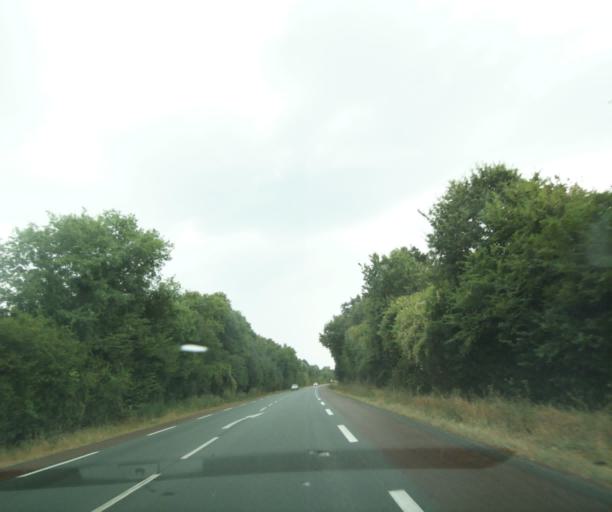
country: FR
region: Poitou-Charentes
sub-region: Departement de la Charente-Maritime
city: Cabariot
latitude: 45.9475
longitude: -0.8665
